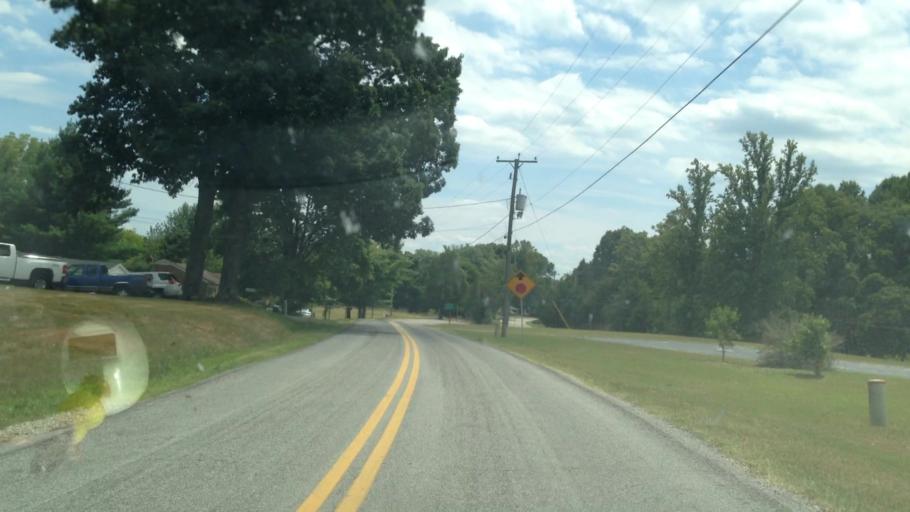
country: US
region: Virginia
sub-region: Henry County
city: Chatmoss
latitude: 36.5985
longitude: -79.8551
